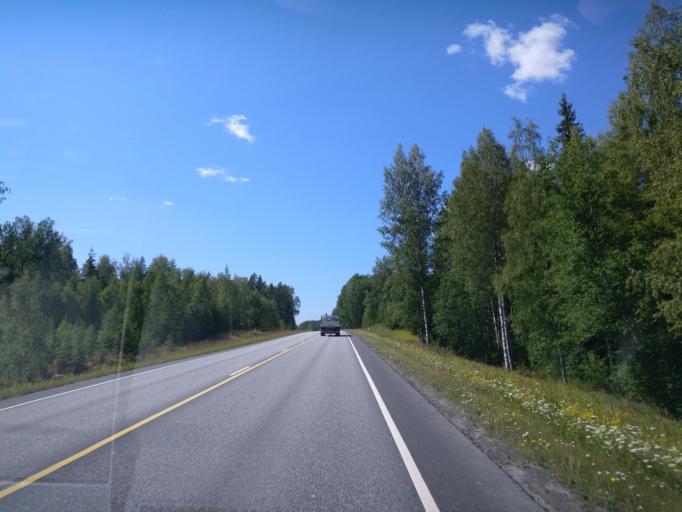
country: FI
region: Satakunta
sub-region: Pori
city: Kullaa
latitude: 61.4613
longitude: 22.1143
